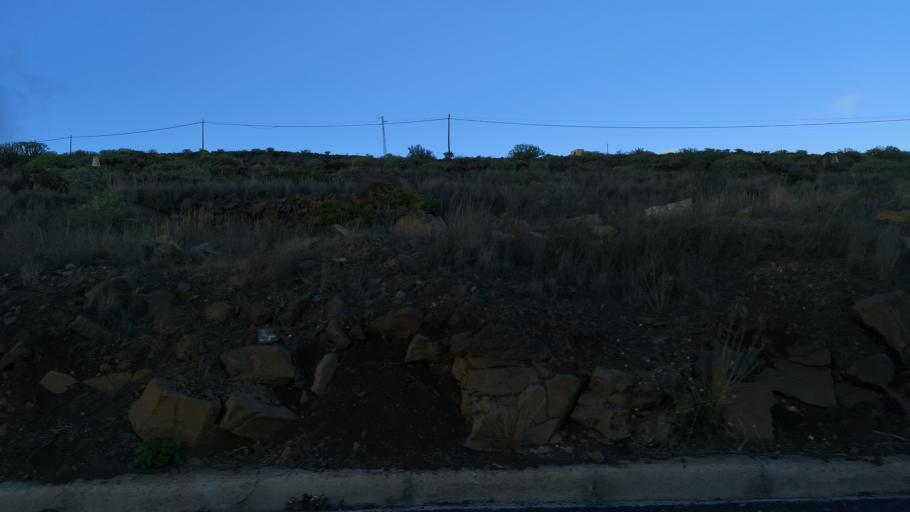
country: ES
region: Canary Islands
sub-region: Provincia de Santa Cruz de Tenerife
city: Alajero
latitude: 28.0451
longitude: -17.2298
